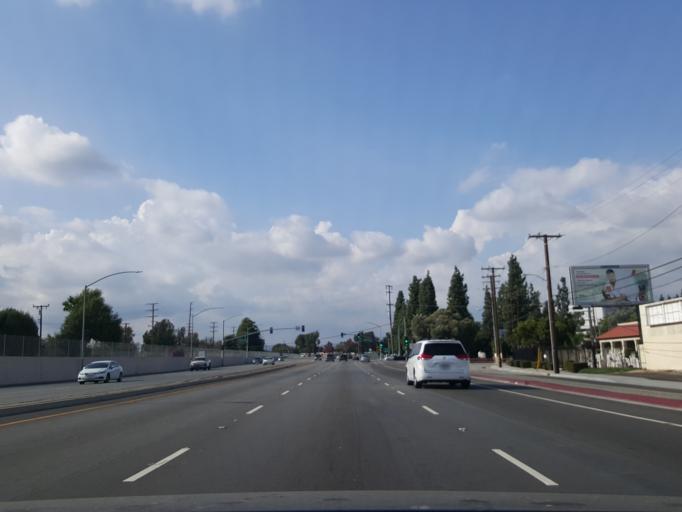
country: US
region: California
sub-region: Los Angeles County
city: Rosemead
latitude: 34.0670
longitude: -118.0694
